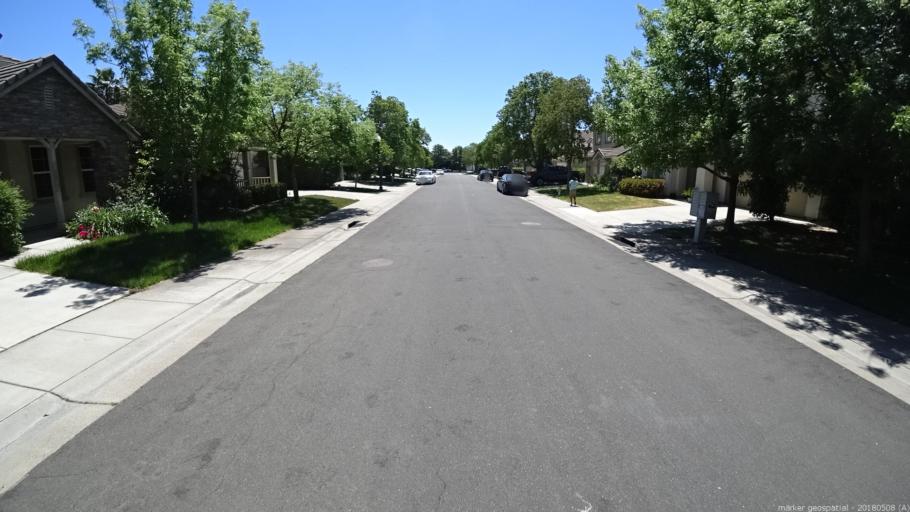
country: US
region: California
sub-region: Sacramento County
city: Elverta
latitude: 38.6783
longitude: -121.5262
